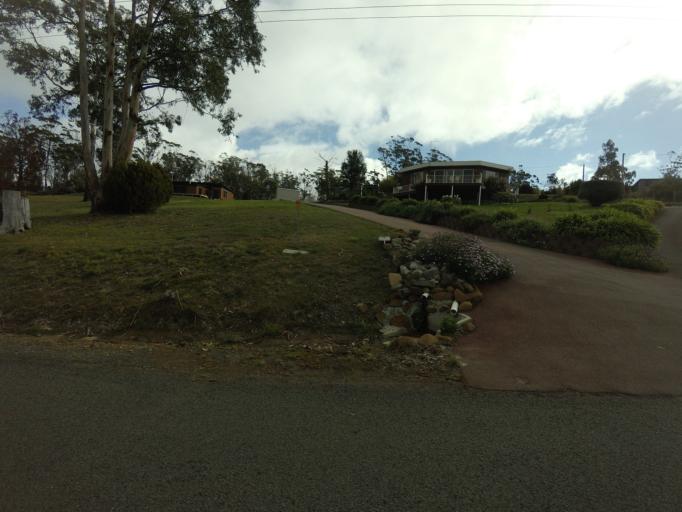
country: AU
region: Tasmania
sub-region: Sorell
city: Sorell
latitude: -42.5401
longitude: 147.9110
